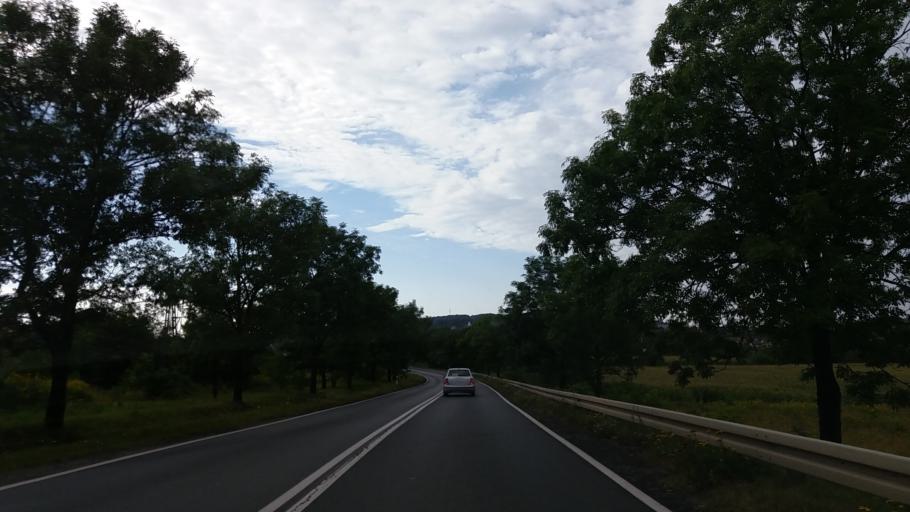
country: PL
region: Lower Silesian Voivodeship
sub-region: Powiat swidnicki
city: Strzegom
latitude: 50.9513
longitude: 16.3584
